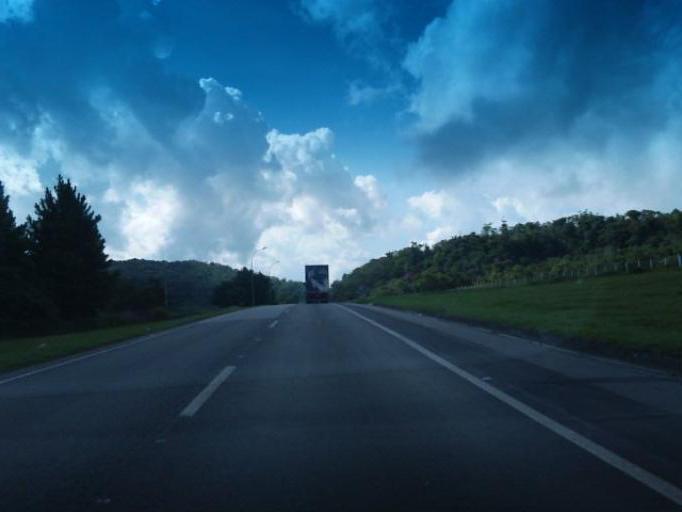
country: BR
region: Parana
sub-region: Campina Grande Do Sul
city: Campina Grande do Sul
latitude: -25.1063
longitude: -48.8047
